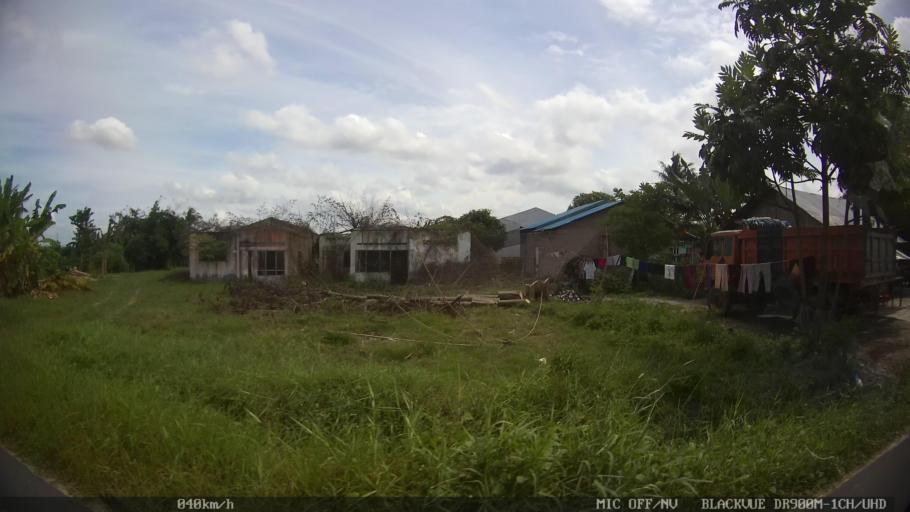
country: ID
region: North Sumatra
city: Percut
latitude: 3.5892
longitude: 98.8654
